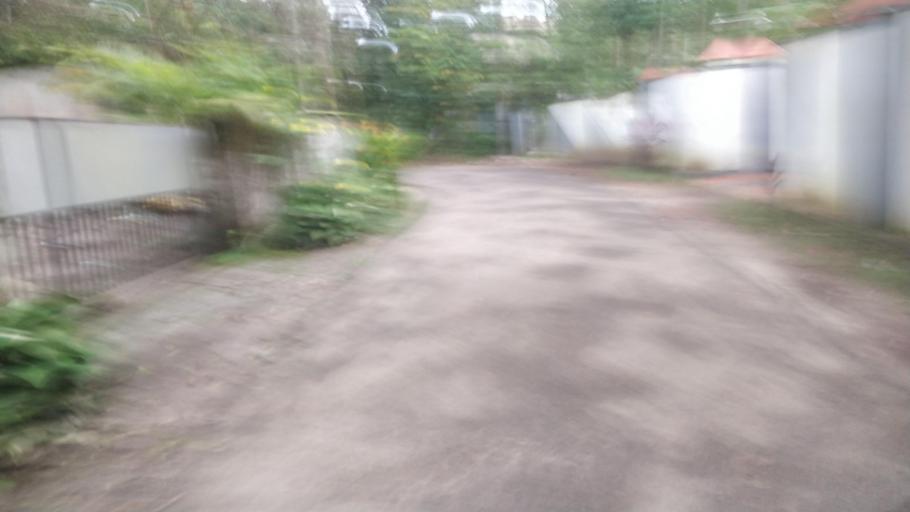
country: IN
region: Kerala
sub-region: Alappuzha
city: Vayalar
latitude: 9.7047
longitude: 76.3526
